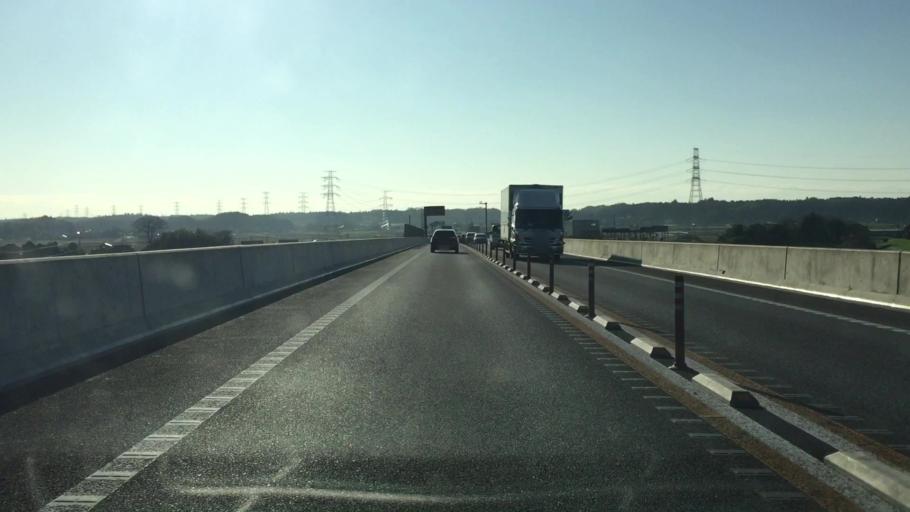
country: JP
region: Ibaraki
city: Inashiki
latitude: 35.9010
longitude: 140.3762
